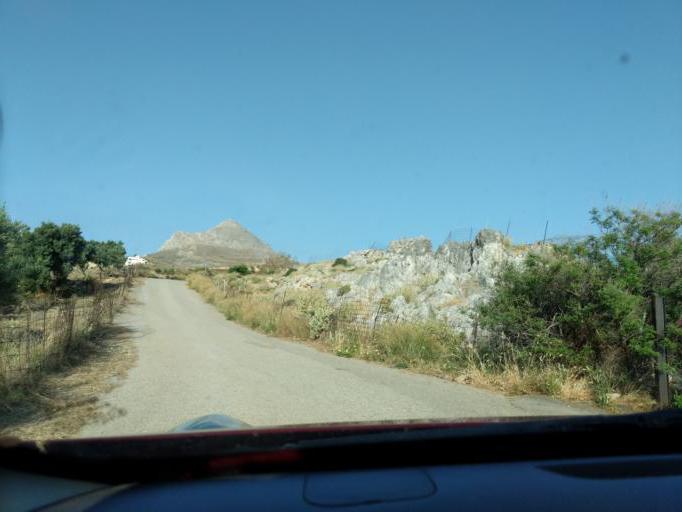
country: GR
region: Crete
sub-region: Nomos Rethymnis
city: Atsipopoulon
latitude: 35.1667
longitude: 24.4256
